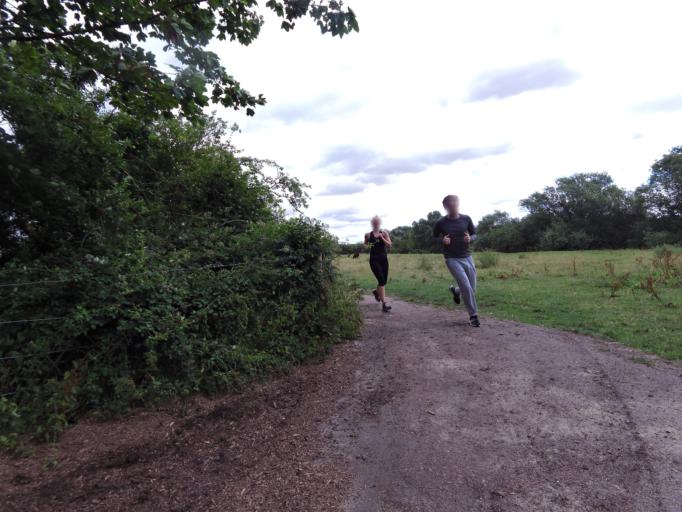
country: GB
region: England
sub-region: Cambridgeshire
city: Grantchester
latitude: 52.1857
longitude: 0.0998
